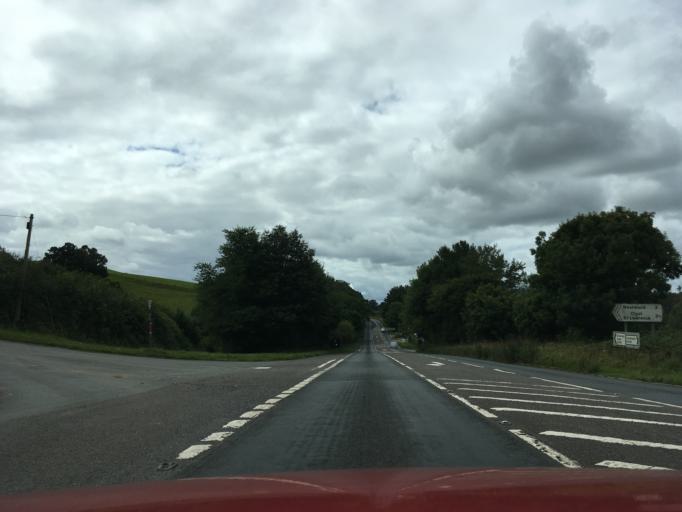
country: GB
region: England
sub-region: Devon
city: Bradninch
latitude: 50.8024
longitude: -3.4342
